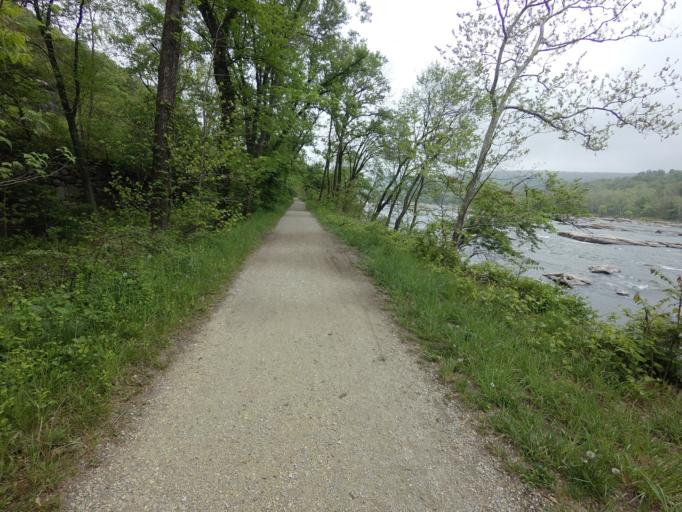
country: US
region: West Virginia
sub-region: Jefferson County
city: Bolivar
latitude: 39.3238
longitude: -77.7210
